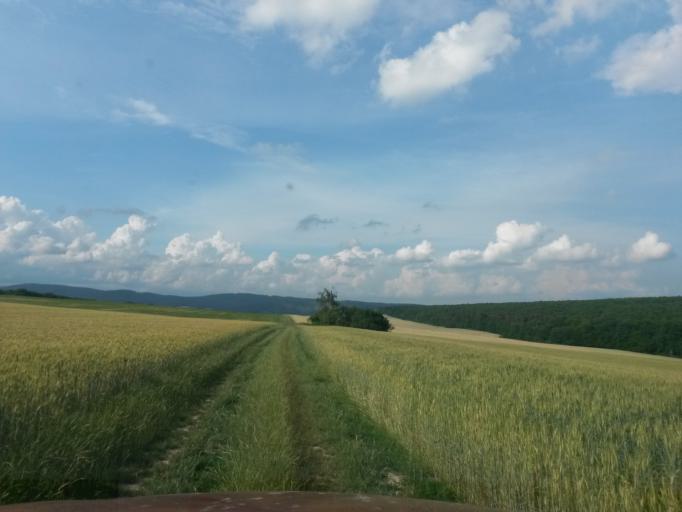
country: SK
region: Kosicky
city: Moldava nad Bodvou
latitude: 48.6323
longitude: 21.1056
